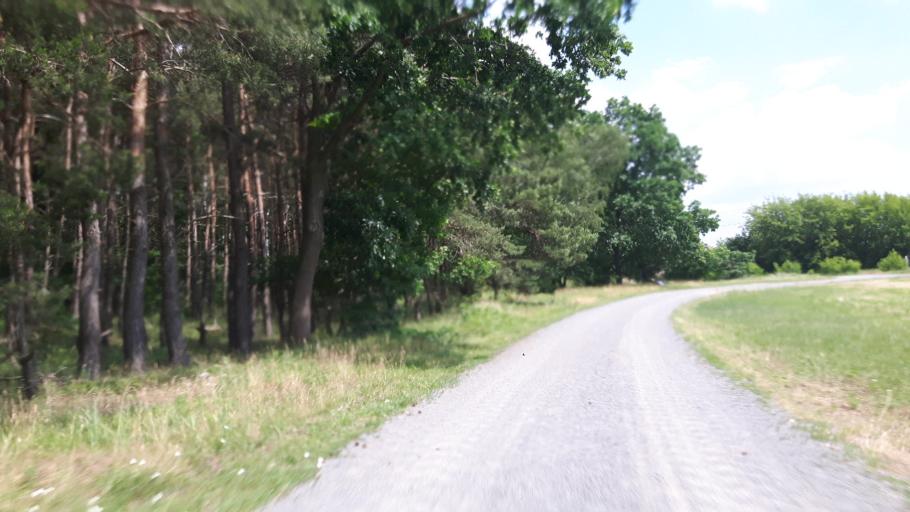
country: DE
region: Saxony-Anhalt
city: Radis
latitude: 51.7525
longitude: 12.4987
